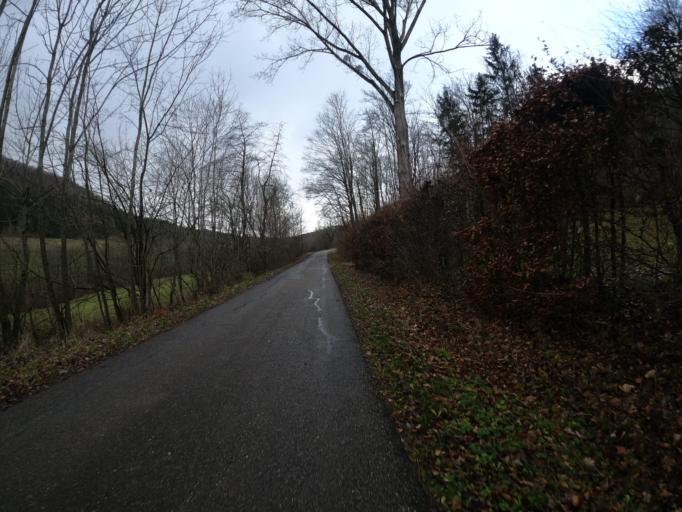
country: DE
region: Baden-Wuerttemberg
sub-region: Regierungsbezirk Stuttgart
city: Waldstetten
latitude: 48.7233
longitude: 9.8469
